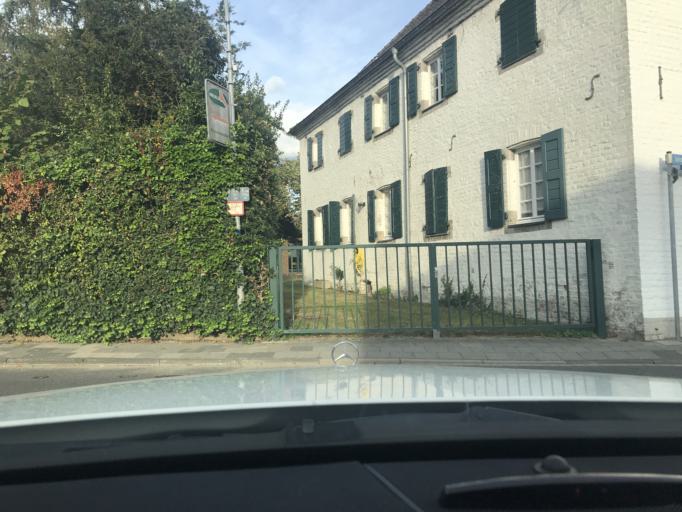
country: DE
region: North Rhine-Westphalia
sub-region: Regierungsbezirk Dusseldorf
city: Neubrueck
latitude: 51.1224
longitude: 6.6837
